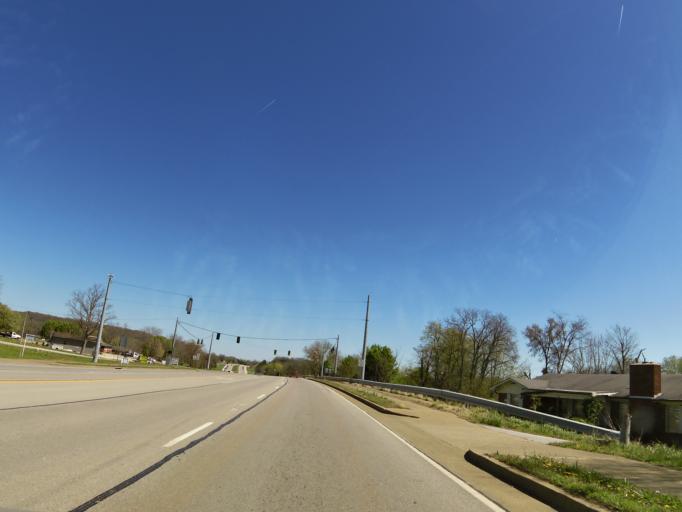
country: US
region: Kentucky
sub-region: Warren County
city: Bowling Green
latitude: 36.9301
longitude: -86.5437
